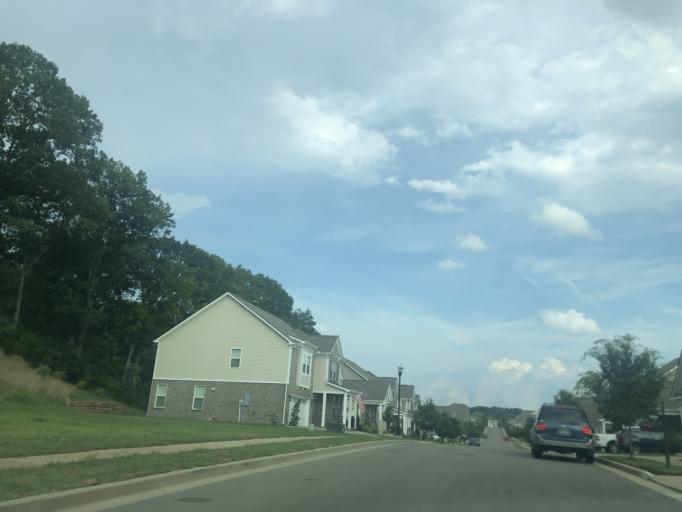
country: US
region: Tennessee
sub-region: Davidson County
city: Lakewood
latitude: 36.1671
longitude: -86.6274
